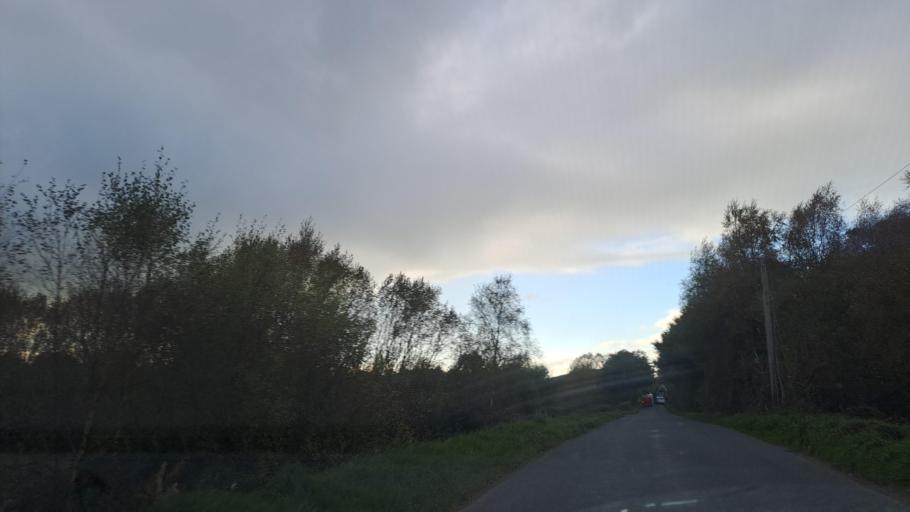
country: IE
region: Ulster
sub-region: County Monaghan
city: Castleblayney
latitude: 54.0377
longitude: -6.8222
